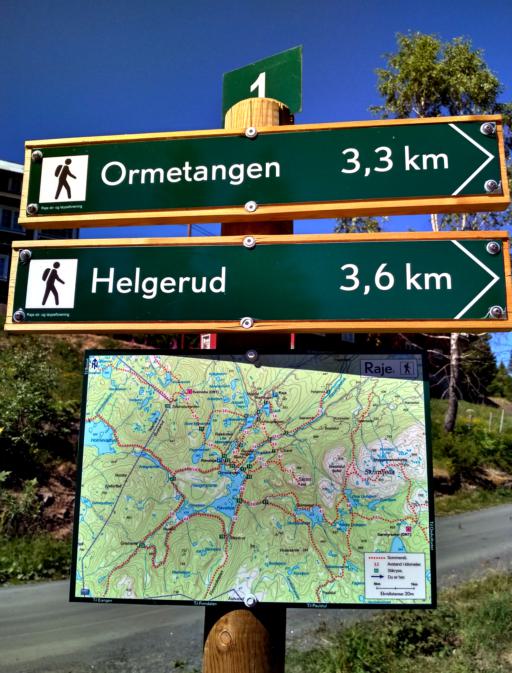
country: NO
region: Buskerud
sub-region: Kongsberg
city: Kongsberg
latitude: 59.5376
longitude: 9.5697
